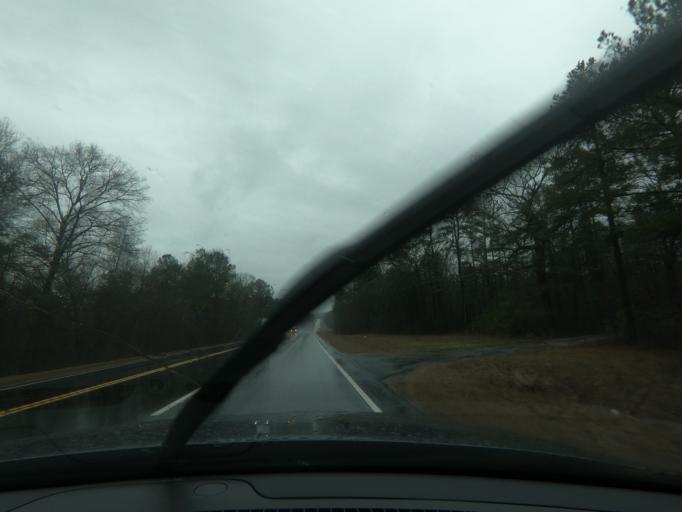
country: US
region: Georgia
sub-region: Bartow County
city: Adairsville
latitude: 34.2976
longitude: -84.8791
